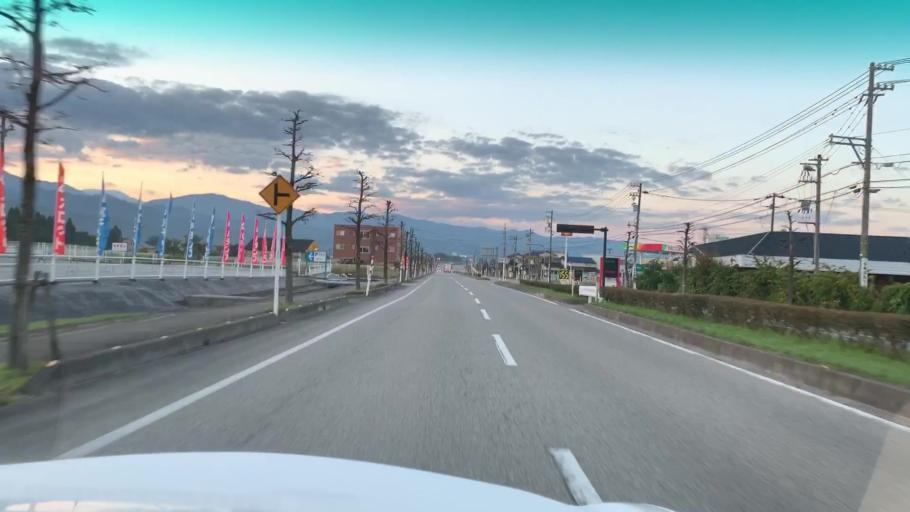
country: JP
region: Toyama
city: Kamiichi
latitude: 36.6994
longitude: 137.3425
